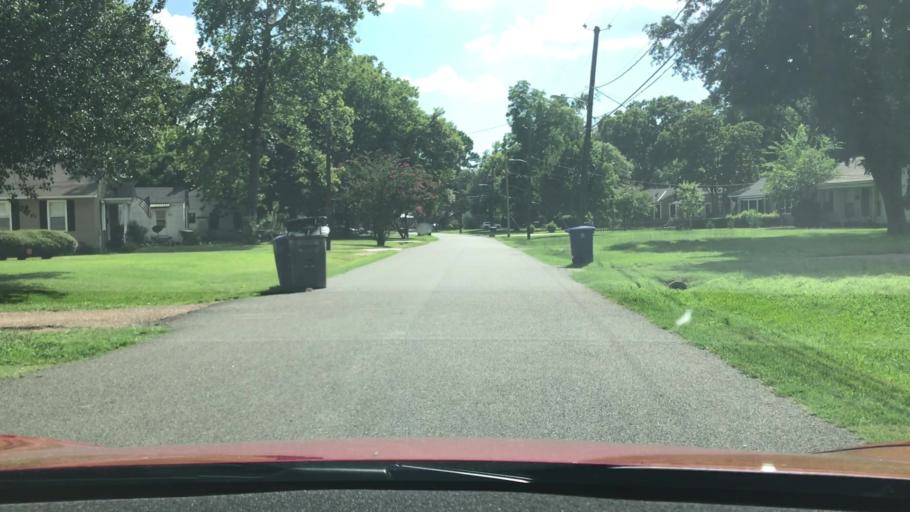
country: US
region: Louisiana
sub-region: Bossier Parish
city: Bossier City
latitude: 32.4703
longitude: -93.7135
